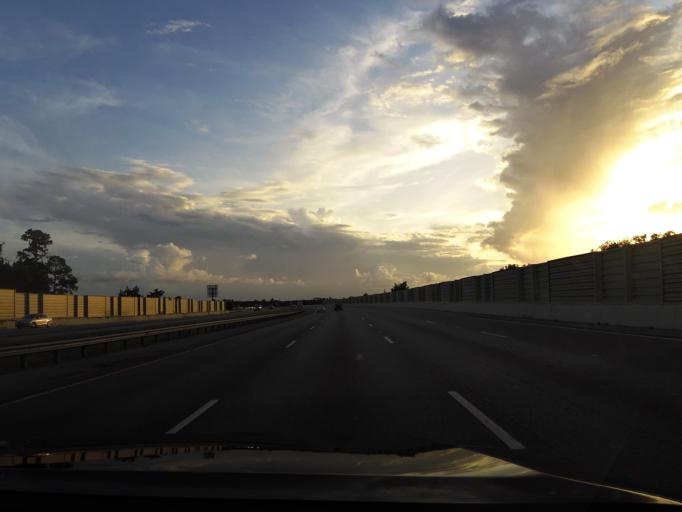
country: US
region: Georgia
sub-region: Glynn County
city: Dock Junction
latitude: 31.2156
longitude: -81.5297
